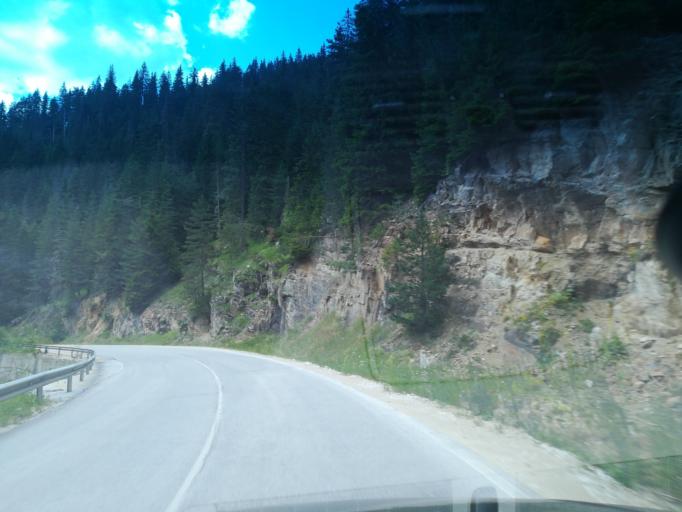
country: BG
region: Smolyan
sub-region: Obshtina Chepelare
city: Chepelare
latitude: 41.6633
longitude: 24.6605
